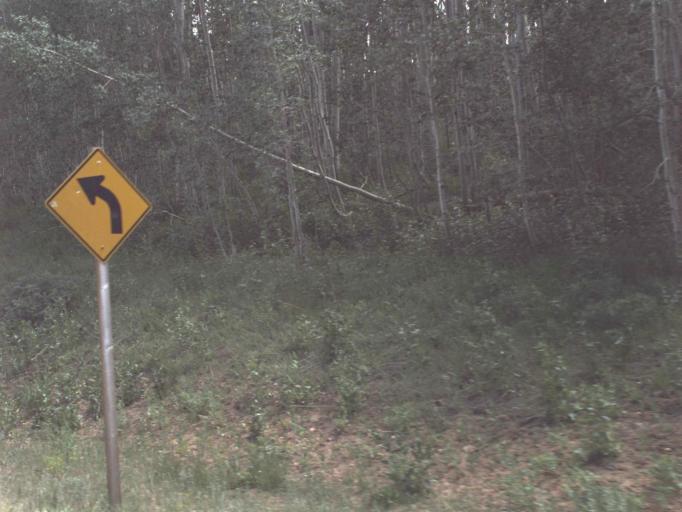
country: US
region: Utah
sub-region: Rich County
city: Randolph
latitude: 41.4755
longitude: -111.4561
